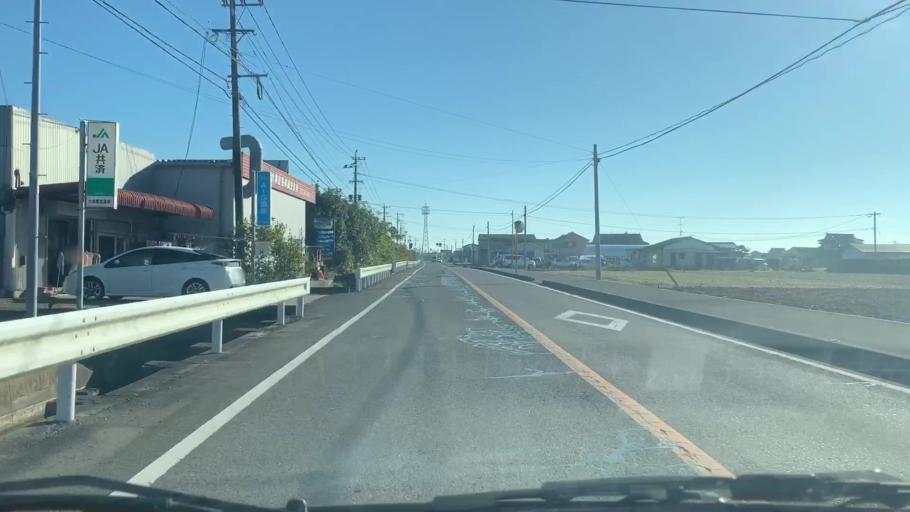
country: JP
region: Saga Prefecture
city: Kashima
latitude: 33.1830
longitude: 130.1758
